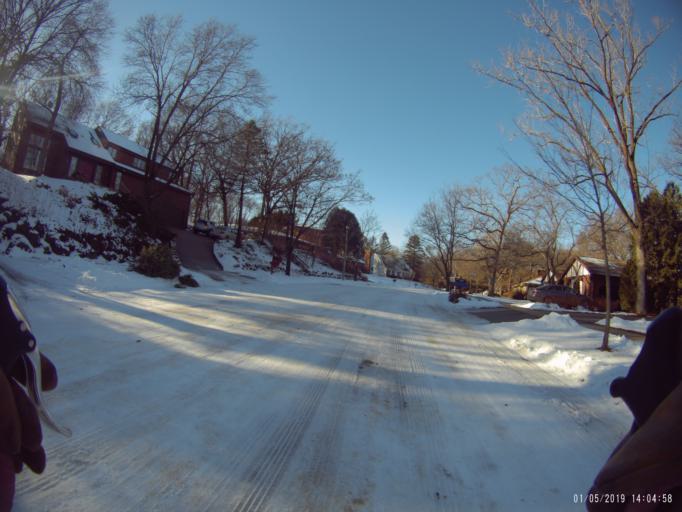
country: US
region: Wisconsin
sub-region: Dane County
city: Shorewood Hills
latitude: 43.0251
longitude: -89.4304
